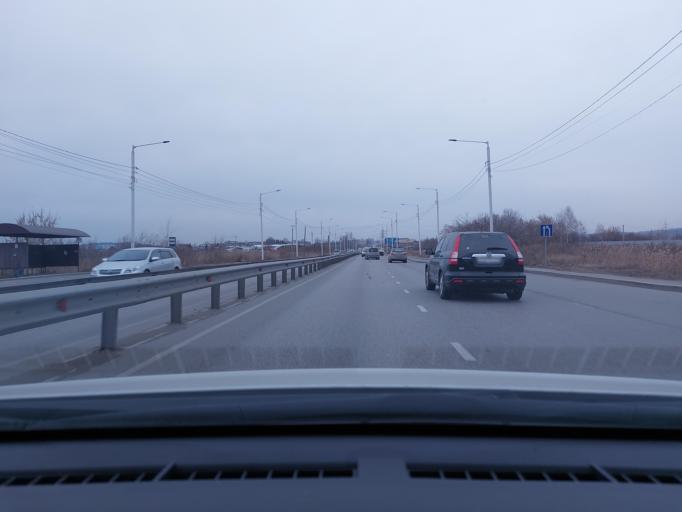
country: RU
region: Irkutsk
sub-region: Irkutskiy Rayon
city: Irkutsk
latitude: 52.3311
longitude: 104.2339
